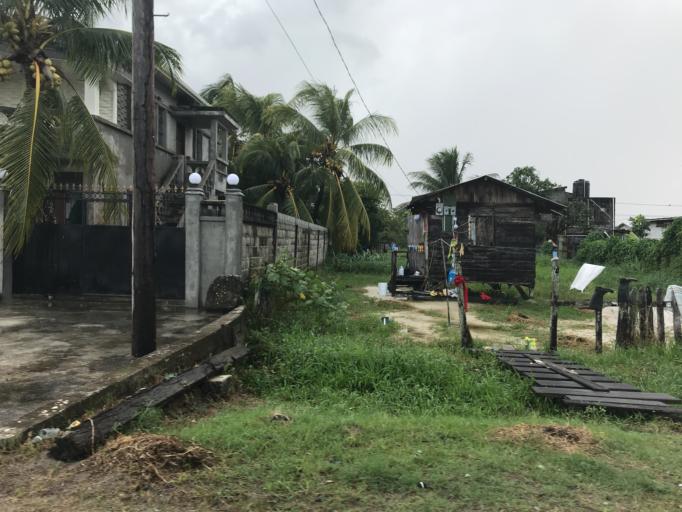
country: GY
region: Demerara-Mahaica
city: Georgetown
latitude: 6.8040
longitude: -58.1198
